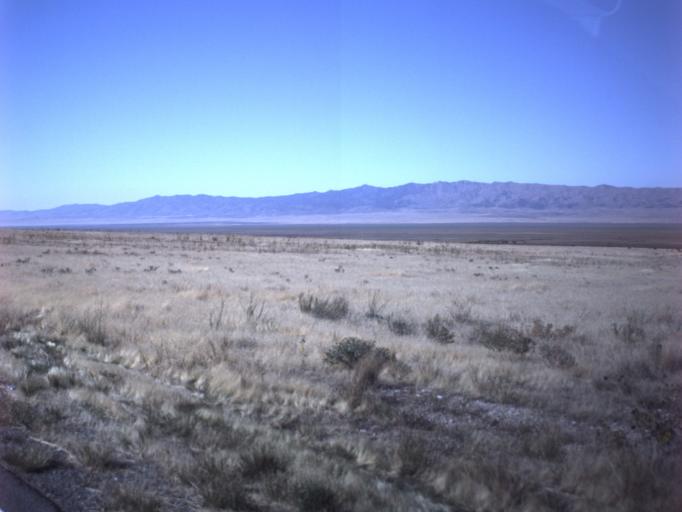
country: US
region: Utah
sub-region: Tooele County
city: Grantsville
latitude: 40.5955
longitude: -112.7172
